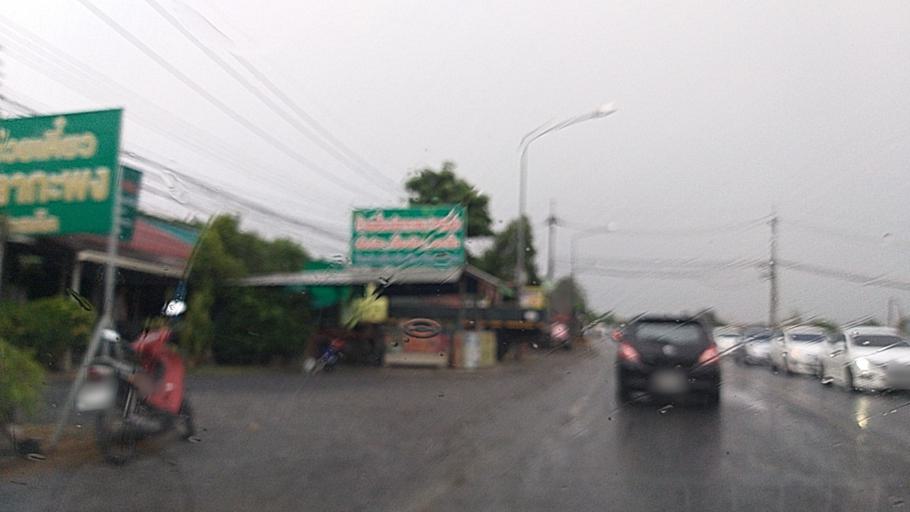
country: TH
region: Phra Nakhon Si Ayutthaya
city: Phra Nakhon Si Ayutthaya
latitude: 14.3438
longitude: 100.5845
